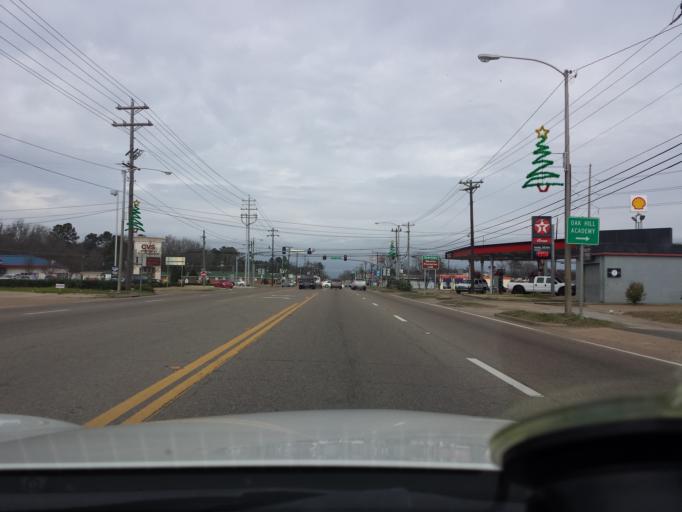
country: US
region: Mississippi
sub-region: Clay County
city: West Point
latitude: 33.6060
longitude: -88.6590
